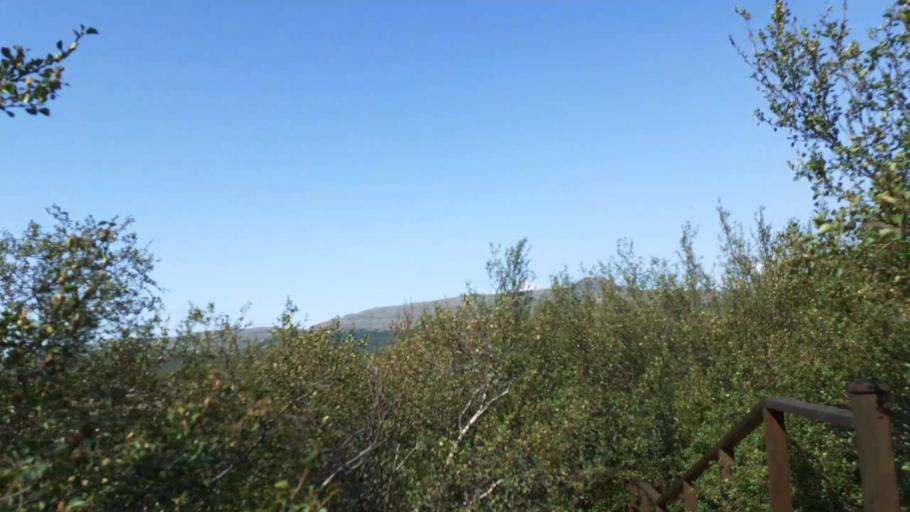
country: IS
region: West
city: Borgarnes
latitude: 64.7516
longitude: -21.5536
